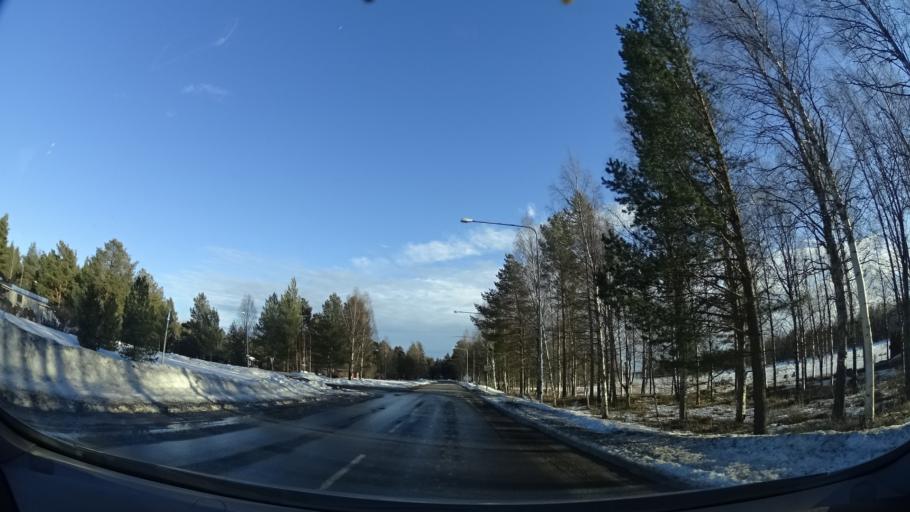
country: SE
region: Vaesterbotten
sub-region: Skelleftea Kommun
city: Byske
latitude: 64.9474
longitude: 21.2273
